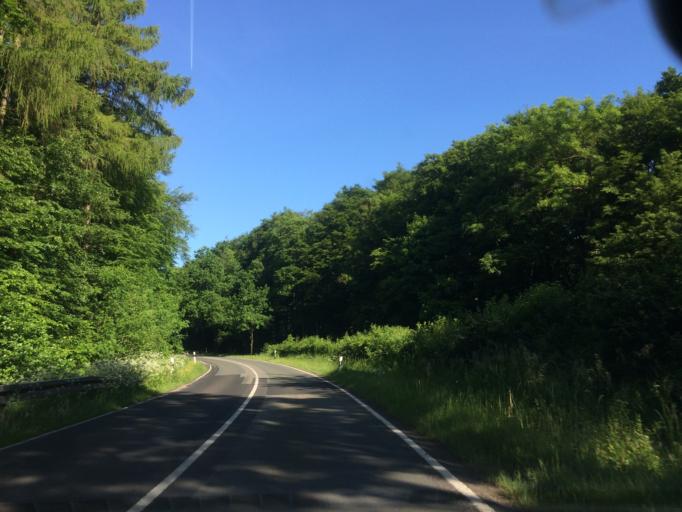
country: DE
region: Hesse
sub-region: Regierungsbezirk Kassel
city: Espenau
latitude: 51.3874
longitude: 9.4356
